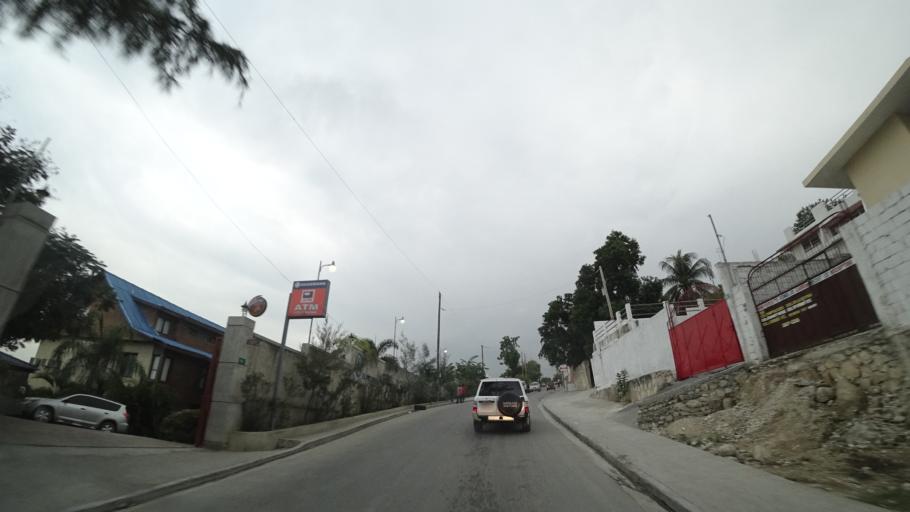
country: HT
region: Ouest
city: Delmas 73
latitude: 18.5669
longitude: -72.2989
